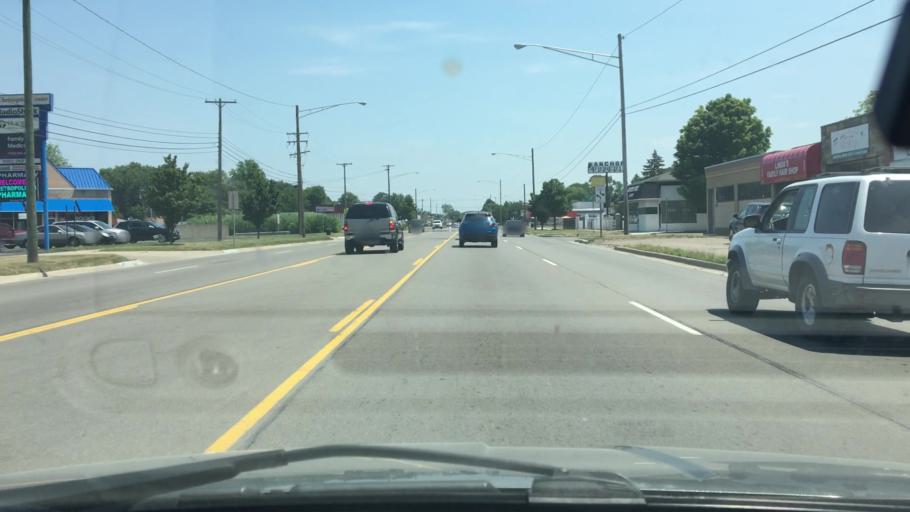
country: US
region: Michigan
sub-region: Wayne County
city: Redford
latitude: 42.3704
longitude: -83.3029
